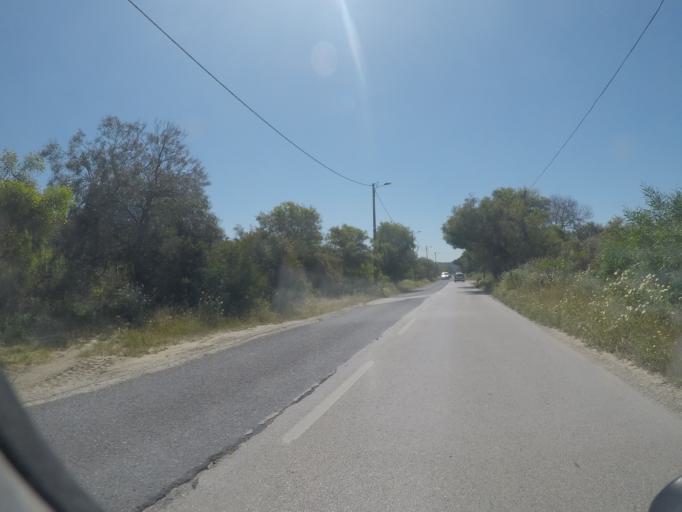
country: PT
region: Setubal
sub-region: Almada
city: Charneca
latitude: 38.6164
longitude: -9.2115
